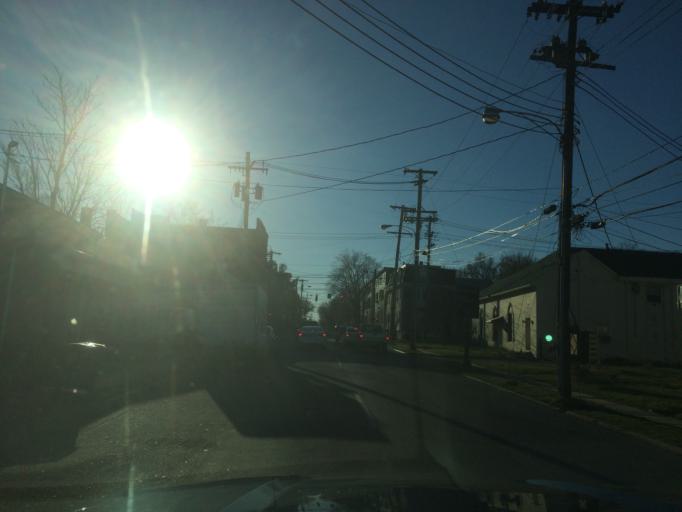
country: US
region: Maryland
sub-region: Frederick County
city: Frederick
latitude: 39.4162
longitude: -77.4043
